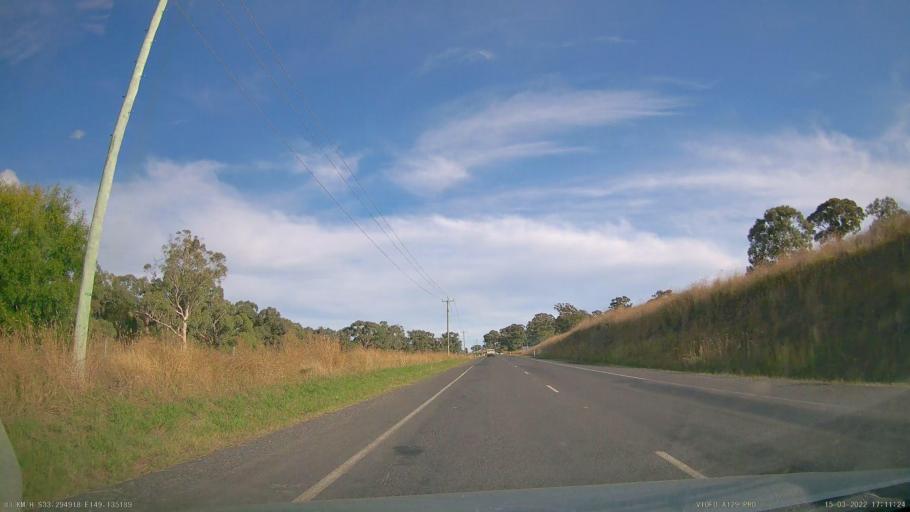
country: AU
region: New South Wales
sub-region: Orange Municipality
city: Orange
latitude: -33.2951
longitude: 149.1352
